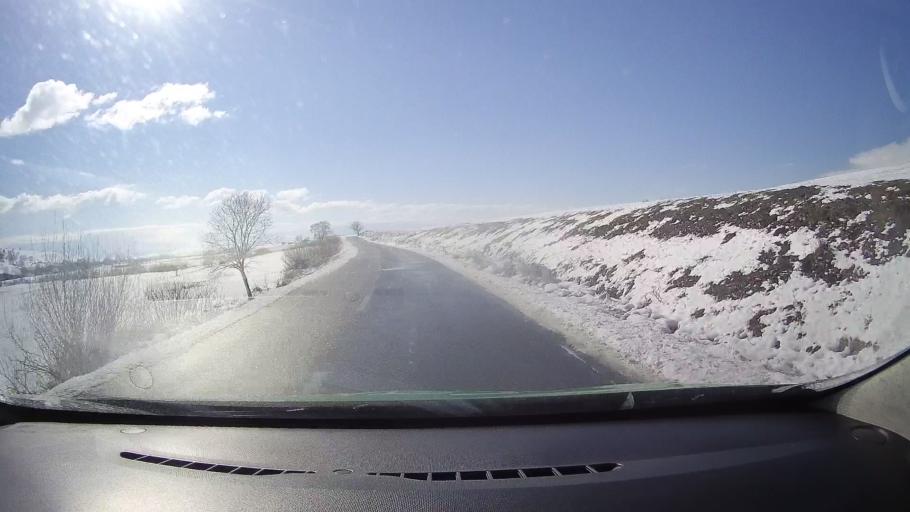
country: RO
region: Sibiu
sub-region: Comuna Rosia
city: Rosia
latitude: 45.8564
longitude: 24.3111
